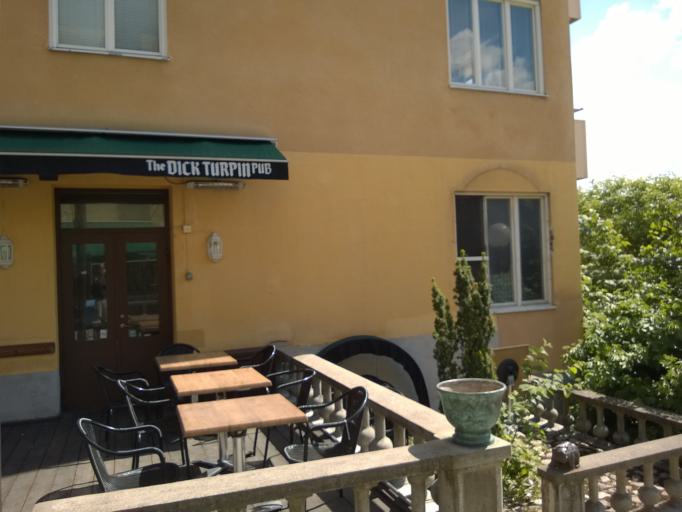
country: SE
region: Stockholm
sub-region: Solna Kommun
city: Solna
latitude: 59.3642
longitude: 17.9947
